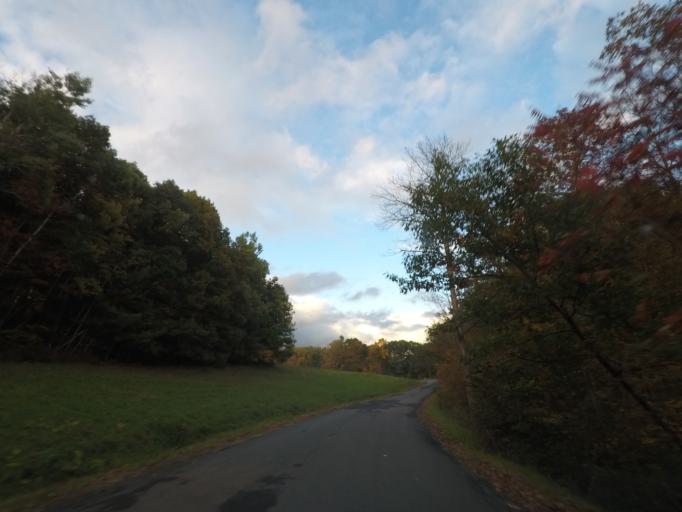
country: US
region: New York
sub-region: Rensselaer County
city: Nassau
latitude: 42.5448
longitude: -73.5846
